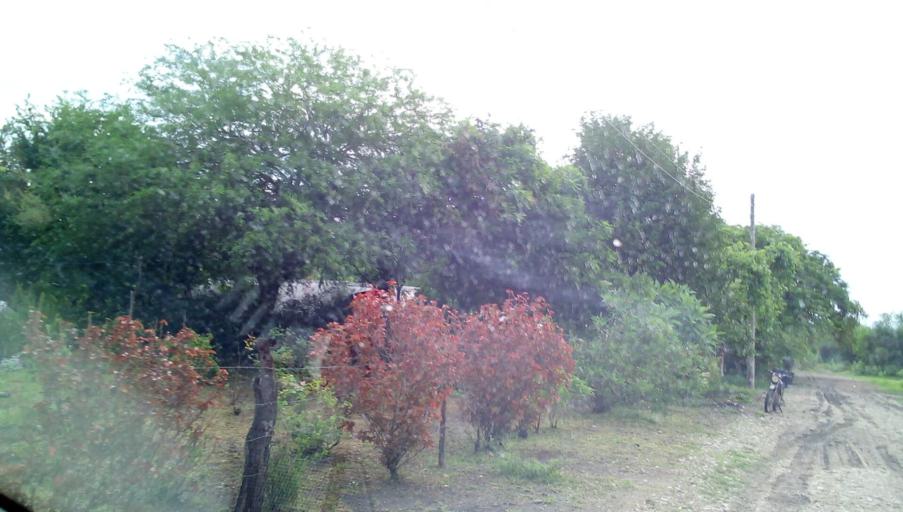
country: MX
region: Veracruz
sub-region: Panuco
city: Guayalejo
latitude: 22.3239
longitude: -98.3350
